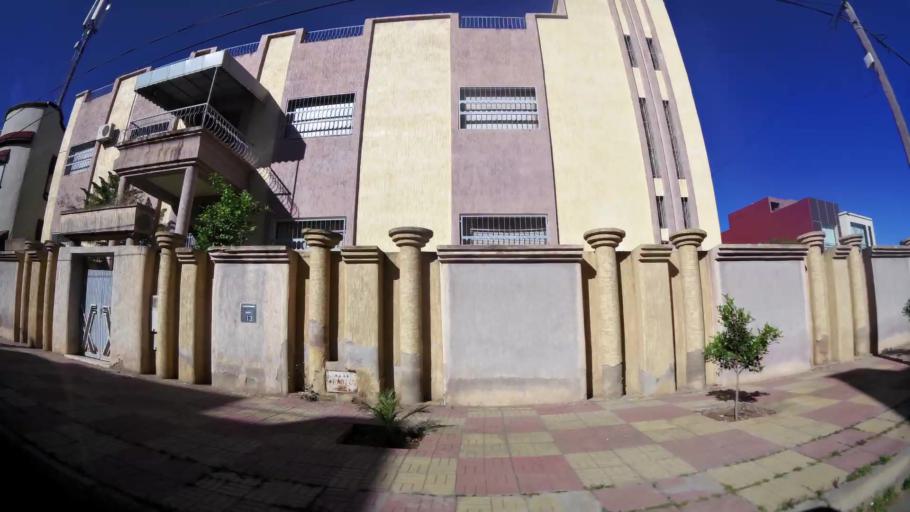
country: MA
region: Oriental
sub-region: Oujda-Angad
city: Oujda
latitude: 34.6593
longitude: -1.9021
